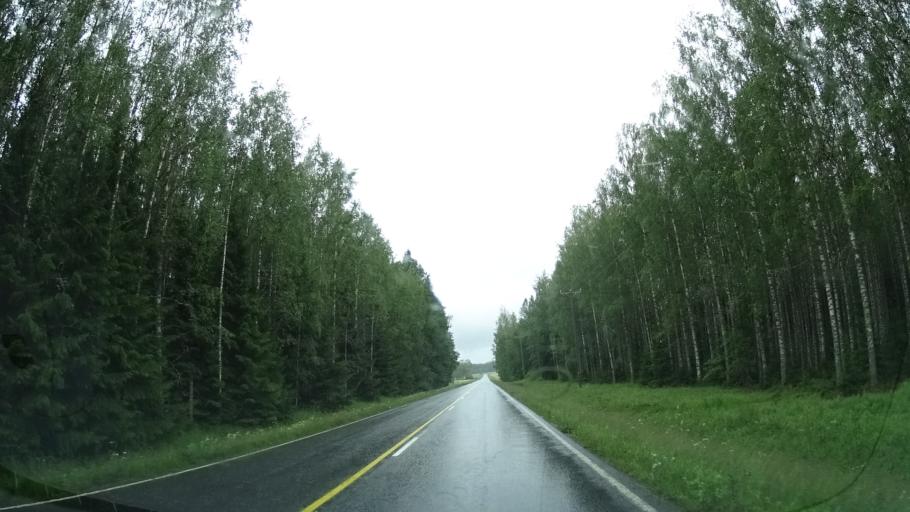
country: FI
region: Haeme
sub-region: Forssa
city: Humppila
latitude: 60.9770
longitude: 23.2527
